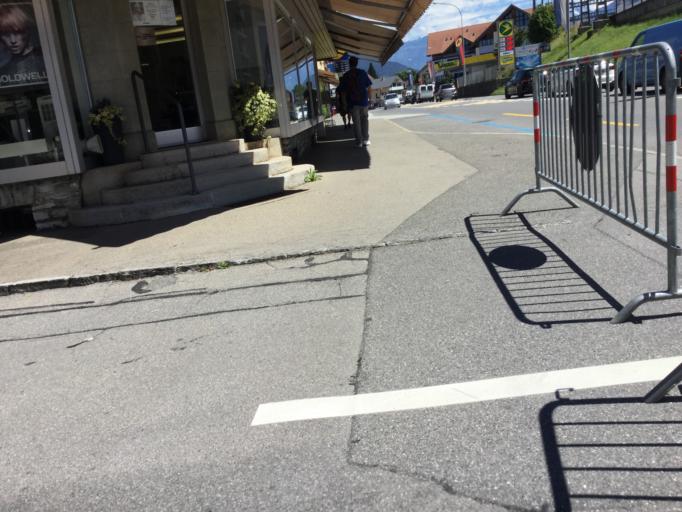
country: CH
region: Bern
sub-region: Frutigen-Niedersimmental District
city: Spiez
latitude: 46.6899
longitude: 7.6718
